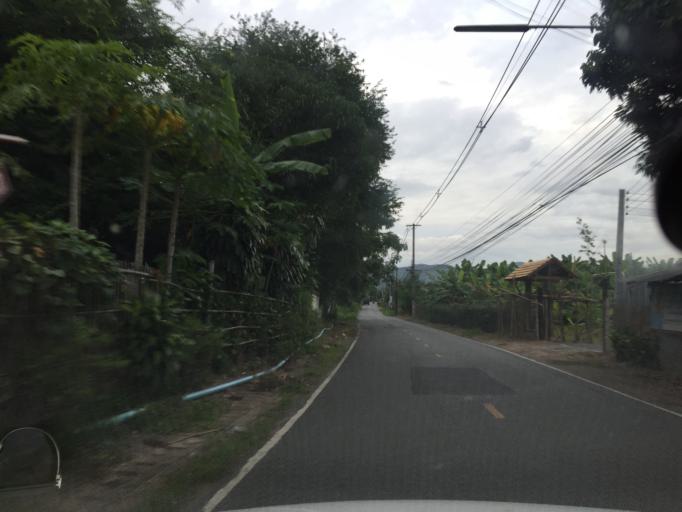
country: TH
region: Chiang Mai
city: San Kamphaeng
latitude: 18.8327
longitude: 99.1636
